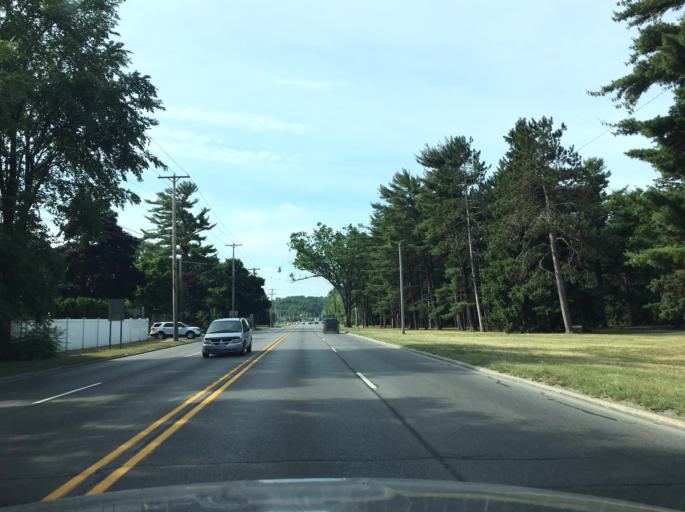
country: US
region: Michigan
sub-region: Grand Traverse County
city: Traverse City
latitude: 44.7552
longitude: -85.6349
